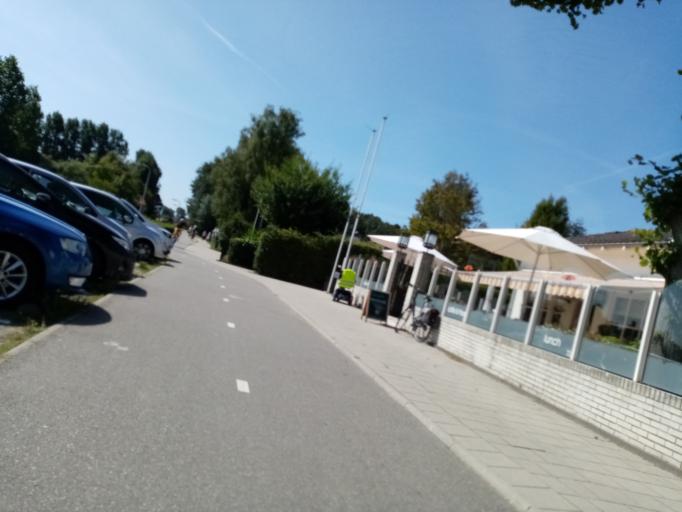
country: NL
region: South Holland
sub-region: Gemeente Noordwijkerhout
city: Noordwijkerhout
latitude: 52.2696
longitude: 4.4674
